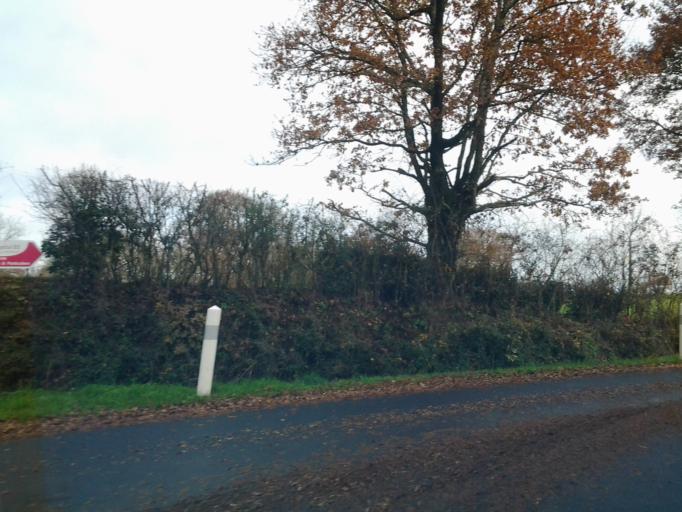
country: FR
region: Pays de la Loire
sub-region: Departement de la Vendee
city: Saint-Florent-des-Bois
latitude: 46.6317
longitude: -1.3056
